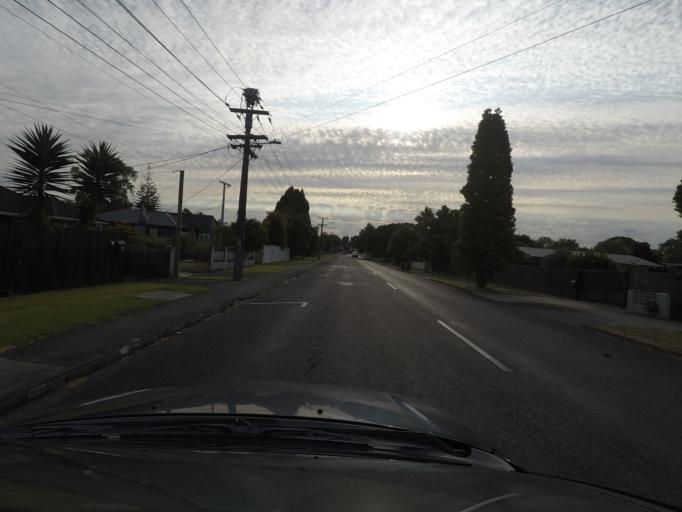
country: NZ
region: Auckland
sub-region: Auckland
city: Rosebank
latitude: -36.8416
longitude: 174.6496
